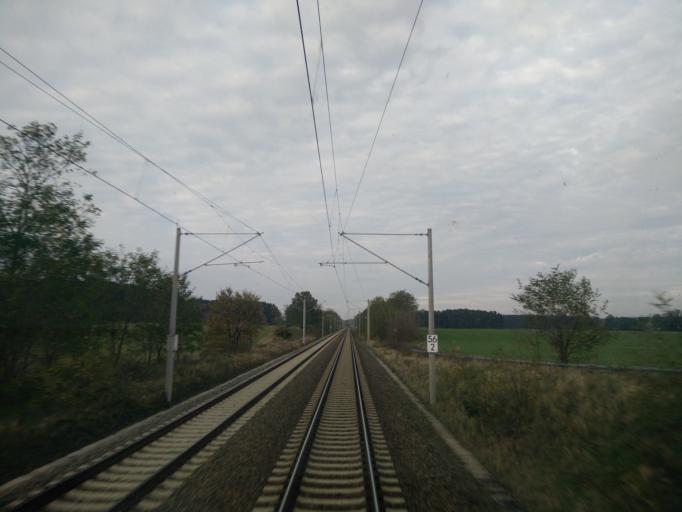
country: DE
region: Brandenburg
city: Halbe
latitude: 52.0607
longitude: 13.7238
